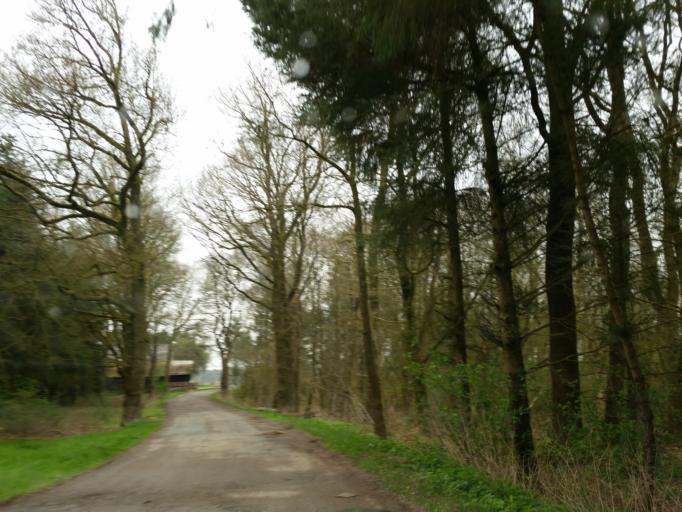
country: DE
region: Lower Saxony
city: Armstorf
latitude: 53.5799
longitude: 9.0109
